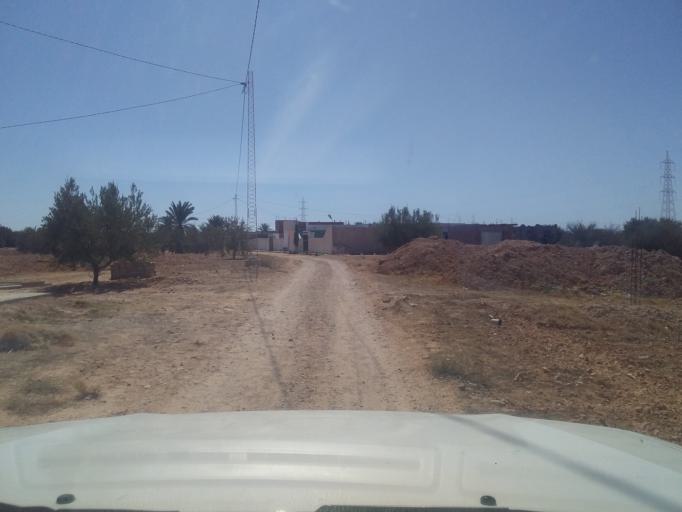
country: TN
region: Qabis
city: Matmata
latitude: 33.5811
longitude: 10.2801
